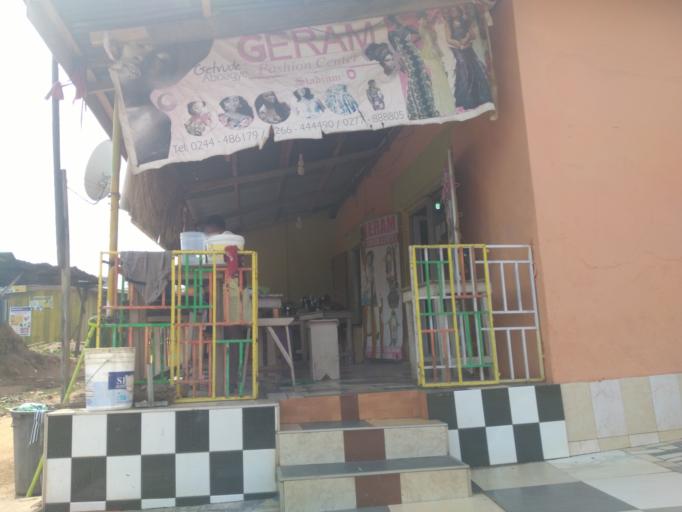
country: GH
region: Ashanti
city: Kumasi
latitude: 6.6851
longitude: -1.6011
